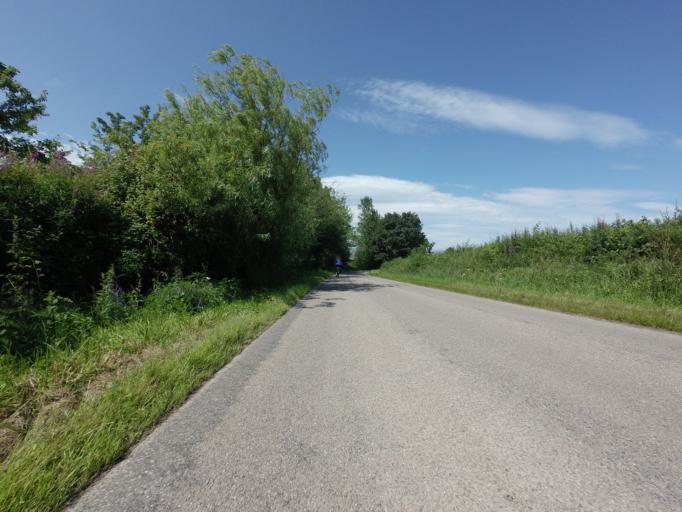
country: GB
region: Scotland
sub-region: Highland
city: Conon Bridge
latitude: 57.5539
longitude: -4.4069
